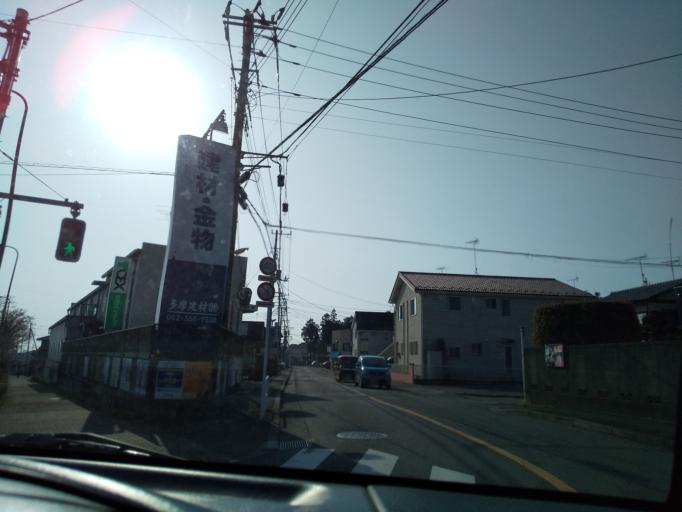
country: JP
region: Tokyo
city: Fussa
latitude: 35.7392
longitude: 139.2864
